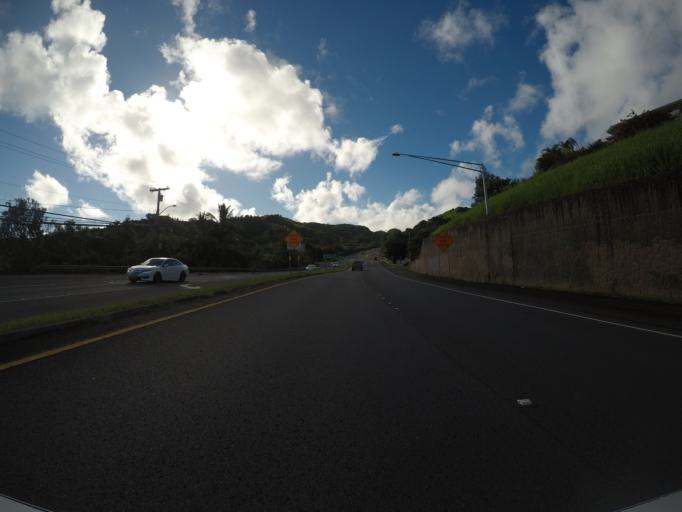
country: US
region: Hawaii
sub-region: Honolulu County
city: Kane'ohe
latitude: 21.4109
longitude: -157.7735
